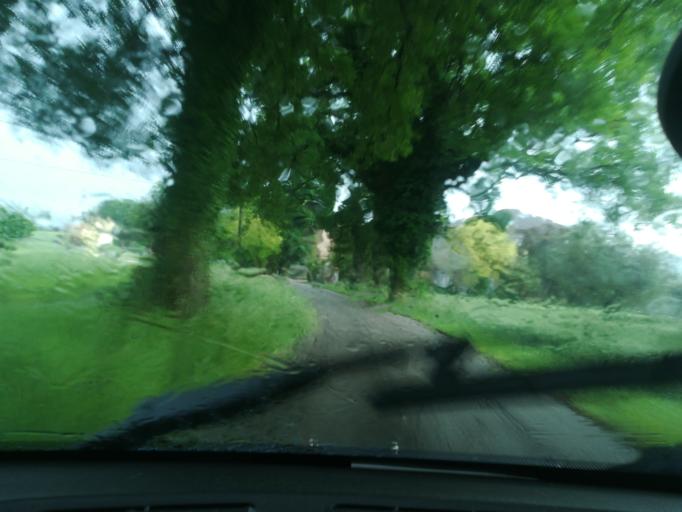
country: IT
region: The Marches
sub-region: Provincia di Macerata
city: Treia
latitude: 43.3070
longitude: 13.3295
